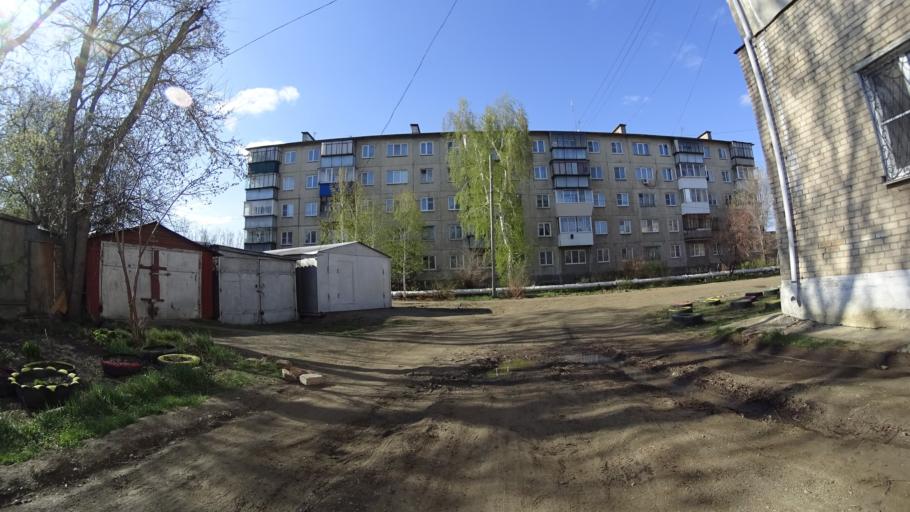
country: RU
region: Chelyabinsk
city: Troitsk
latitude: 54.1048
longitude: 61.5573
